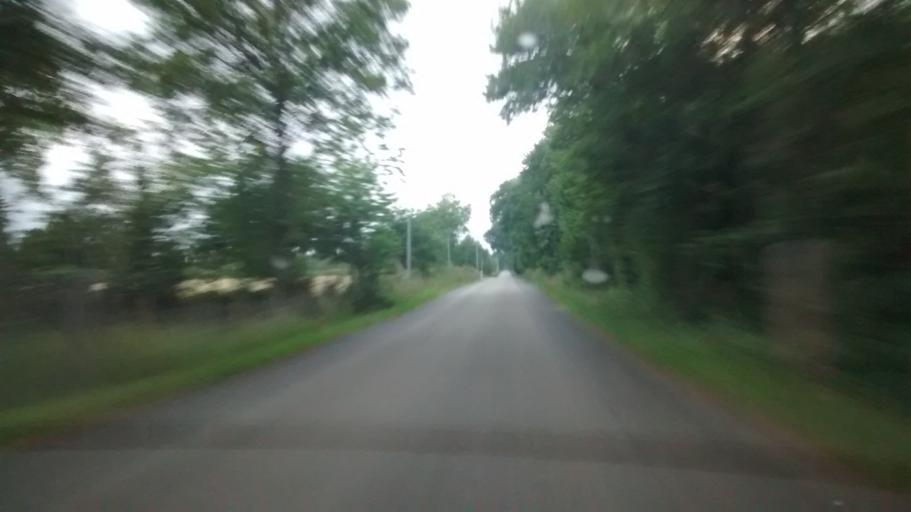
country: FR
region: Brittany
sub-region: Departement du Morbihan
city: Pleucadeuc
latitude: 47.7340
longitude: -2.3296
